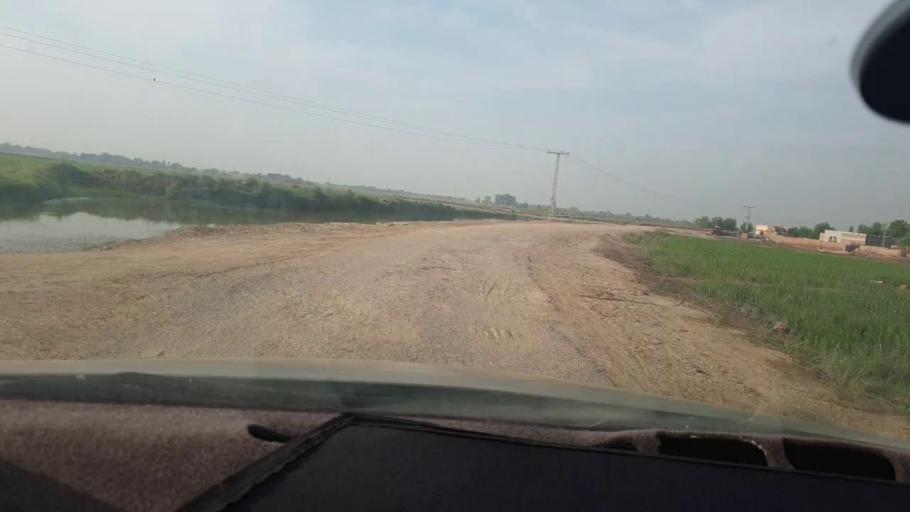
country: PK
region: Balochistan
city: Jhatpat
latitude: 28.3323
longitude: 68.3957
